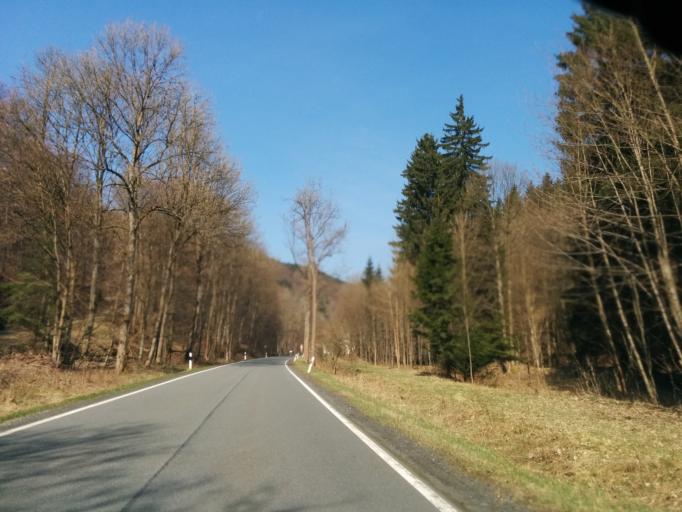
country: DE
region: Lower Saxony
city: Sankt Andreasberg
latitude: 51.6725
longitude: 10.5037
